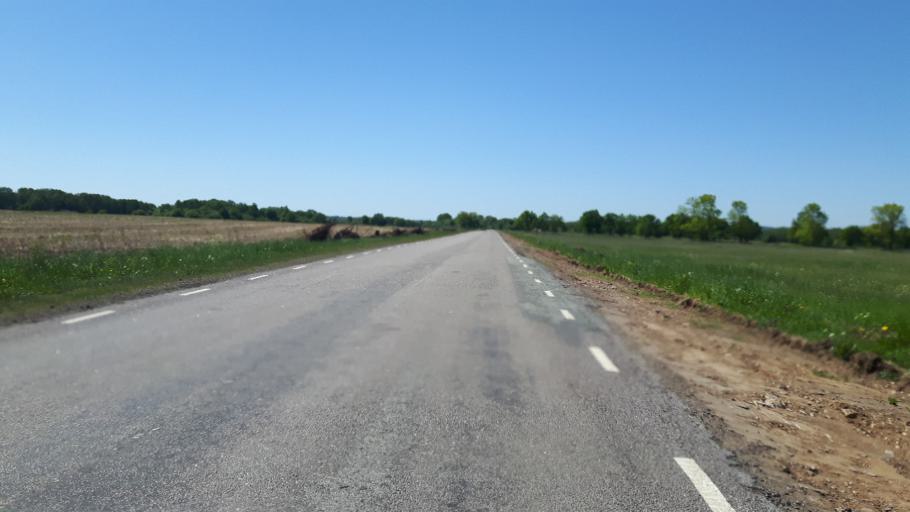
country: EE
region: Ida-Virumaa
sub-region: Narva-Joesuu linn
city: Narva-Joesuu
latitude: 59.3993
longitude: 27.9328
